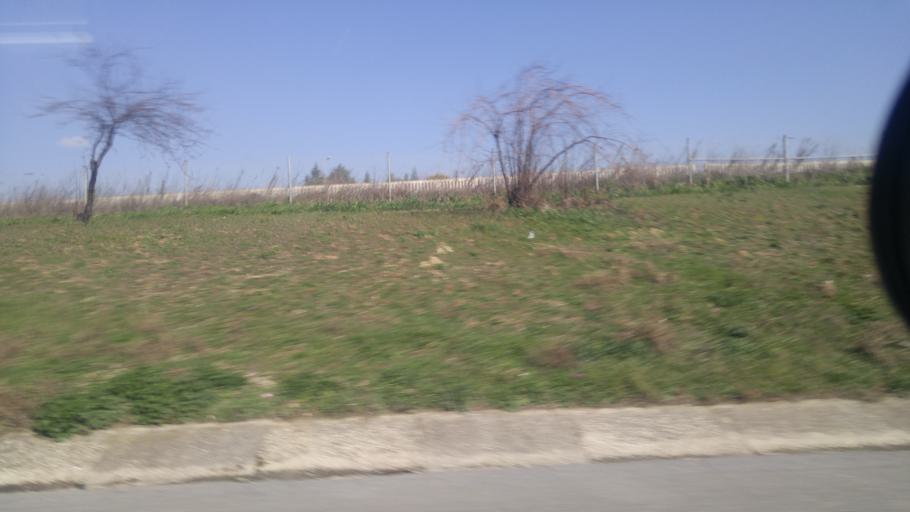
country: TR
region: Istanbul
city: Selimpasa
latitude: 41.0759
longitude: 28.3759
